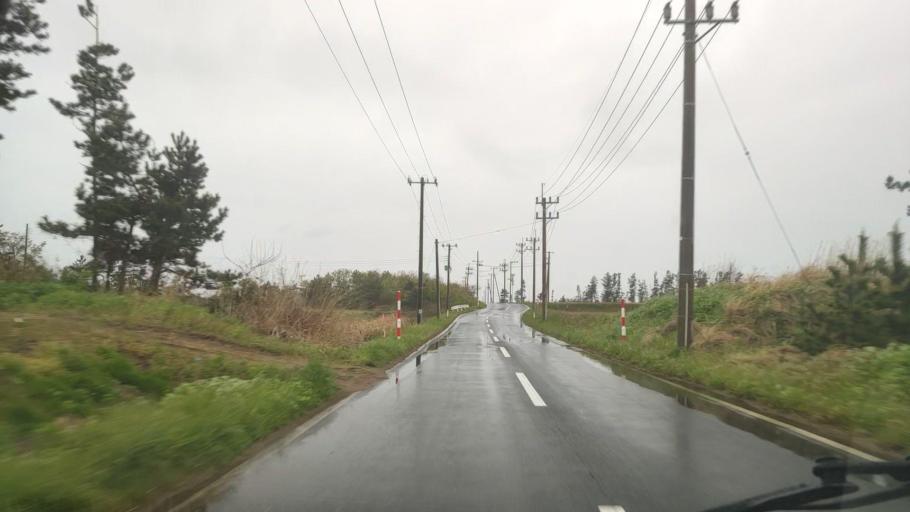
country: JP
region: Akita
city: Noshiromachi
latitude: 40.0952
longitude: 139.9741
